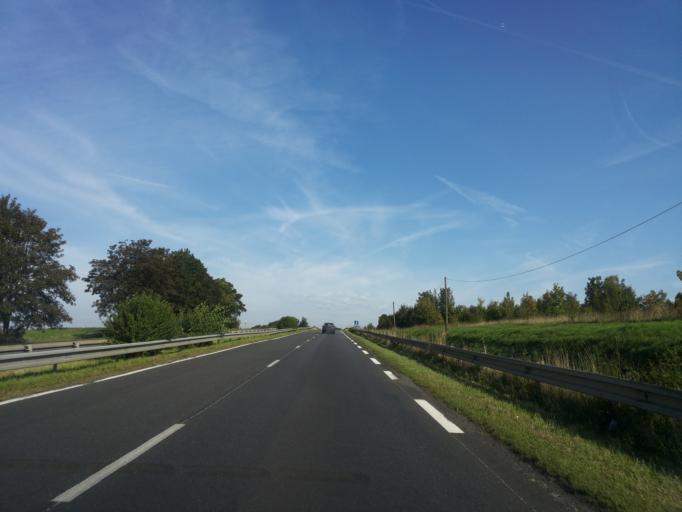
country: FR
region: Picardie
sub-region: Departement de l'Aisne
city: Itancourt
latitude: 49.7872
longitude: 3.3264
